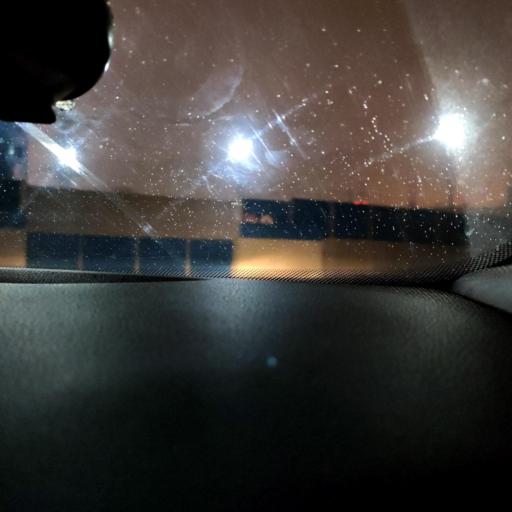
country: RU
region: Moskovskaya
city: Alekseyevka
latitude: 55.6387
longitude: 37.8118
